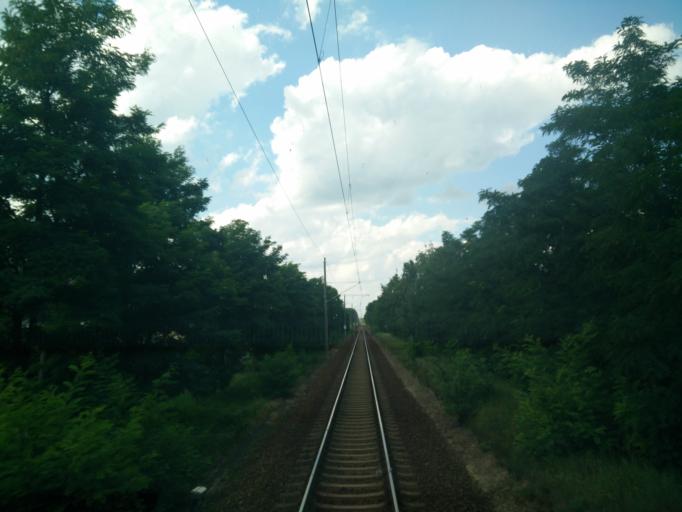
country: DE
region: Brandenburg
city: Vetschau
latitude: 51.8173
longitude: 14.0306
